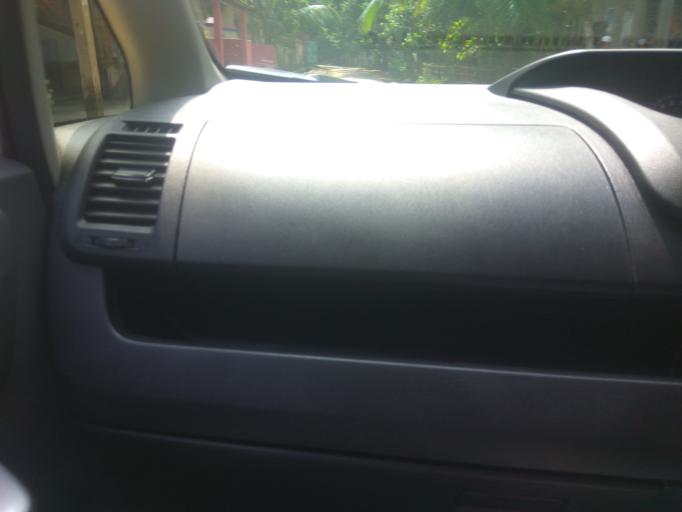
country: IN
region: Assam
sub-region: Karimganj
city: Karimganj
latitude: 24.8130
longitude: 92.1782
